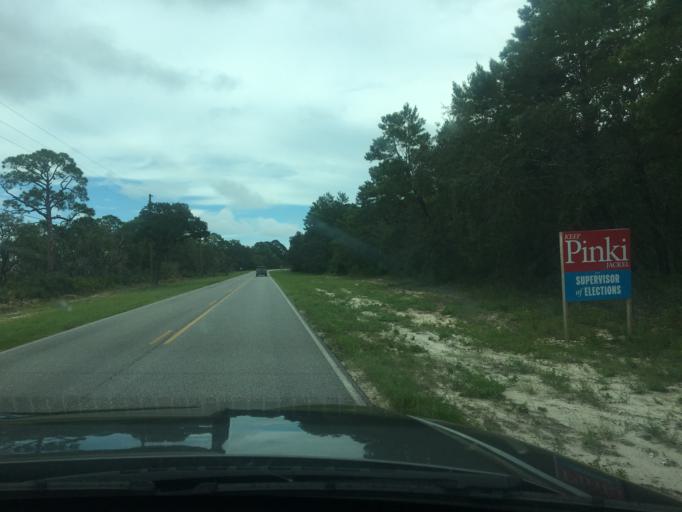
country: US
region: Florida
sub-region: Wakulla County
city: Crawfordville
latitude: 29.9039
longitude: -84.3518
